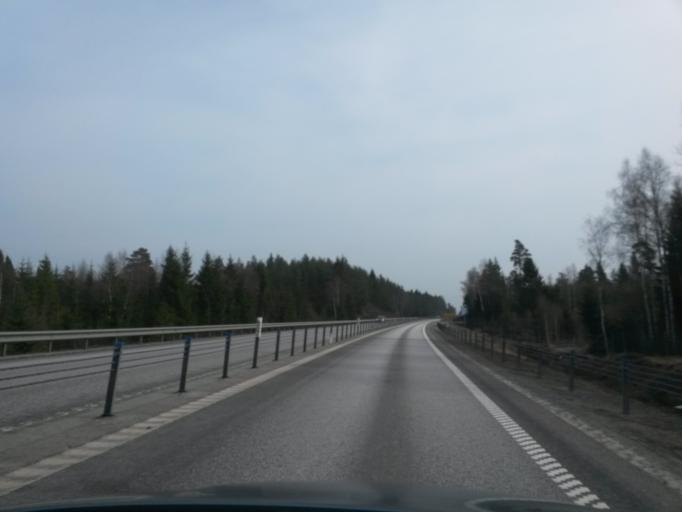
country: SE
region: Vaestra Goetaland
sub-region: Gullspangs Kommun
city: Anderstorp
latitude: 58.9064
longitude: 14.3506
